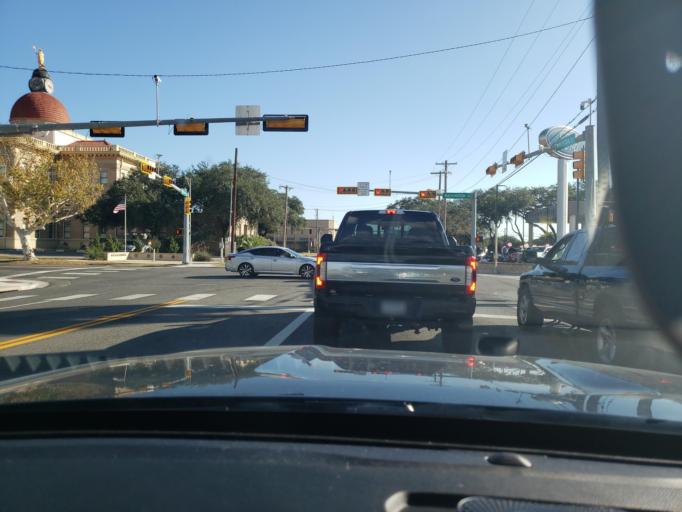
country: US
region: Texas
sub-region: Bee County
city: Beeville
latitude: 28.4006
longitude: -97.7490
